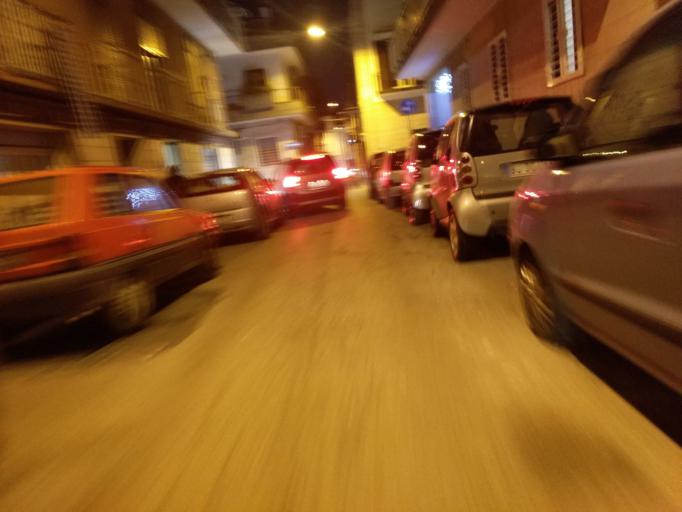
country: IT
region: Apulia
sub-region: Provincia di Bari
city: Modugno
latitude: 41.0818
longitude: 16.7838
